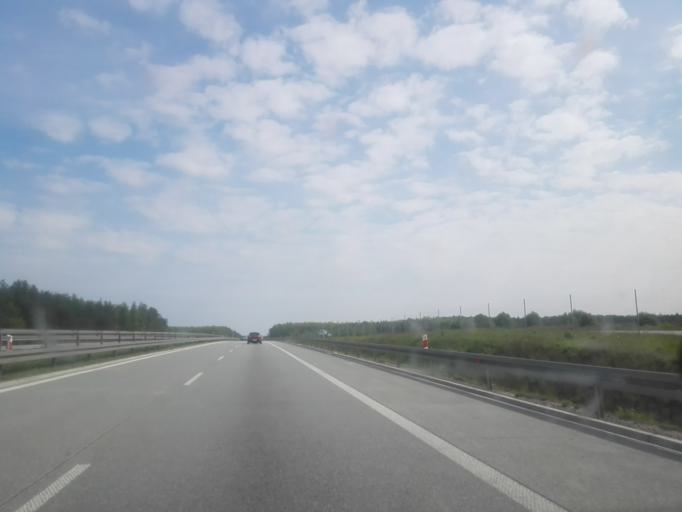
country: PL
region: Lodz Voivodeship
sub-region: Powiat rawski
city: Rawa Mazowiecka
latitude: 51.7150
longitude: 20.2199
